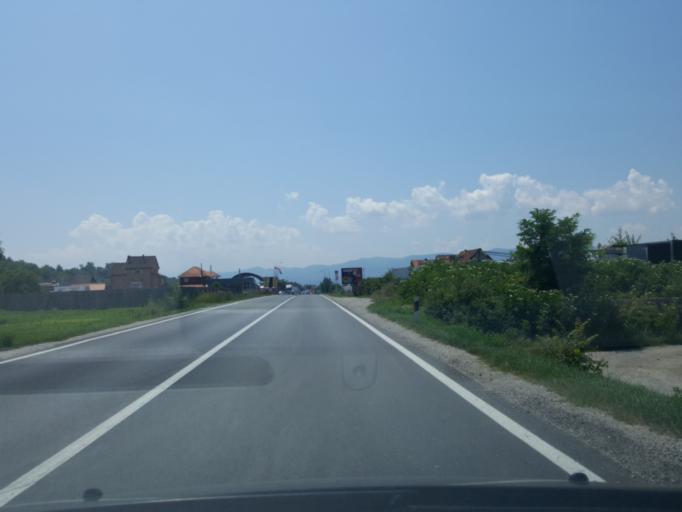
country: RS
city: Prislonica
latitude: 43.9275
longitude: 20.4101
